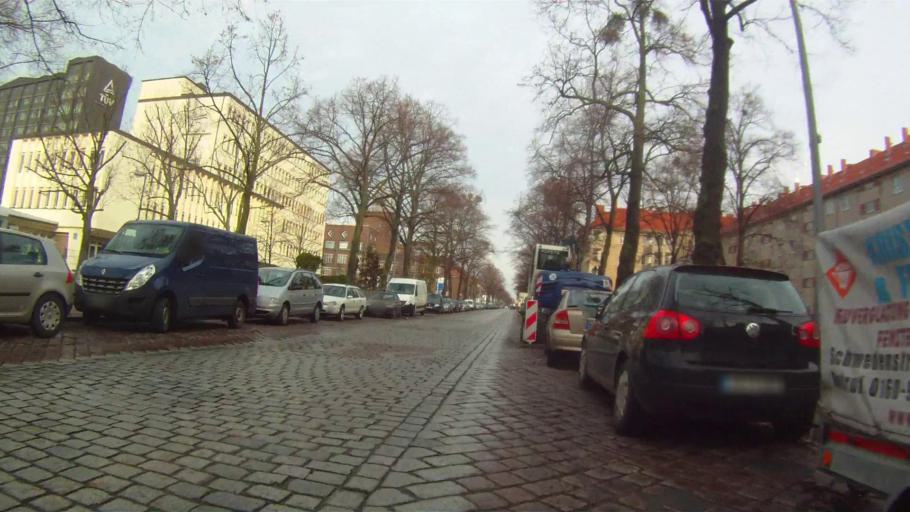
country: DE
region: Berlin
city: Schoneberg Bezirk
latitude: 52.4641
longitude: 13.3702
